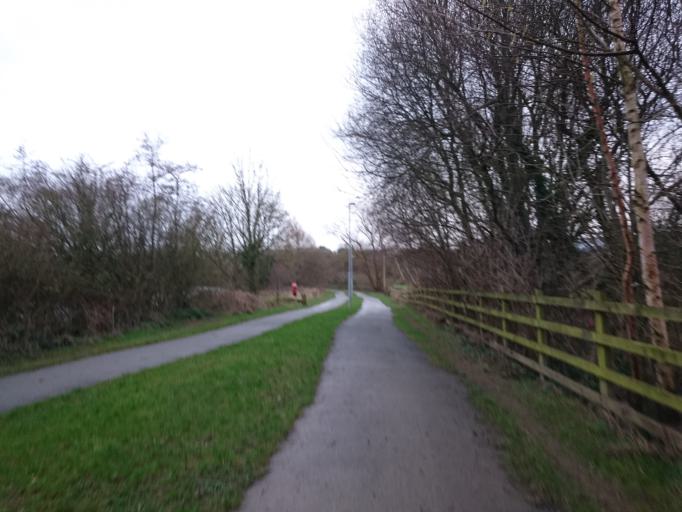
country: IE
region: Leinster
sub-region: Kilkenny
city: Kilkenny
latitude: 52.6708
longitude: -7.2621
